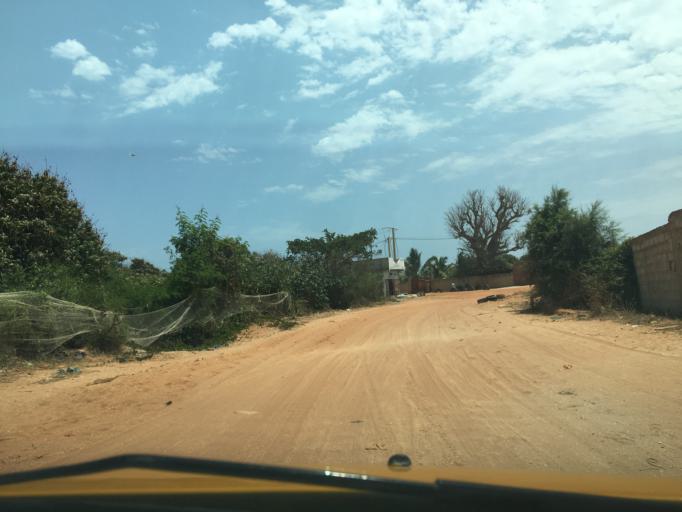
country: SN
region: Thies
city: Thies
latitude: 14.8086
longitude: -17.1900
